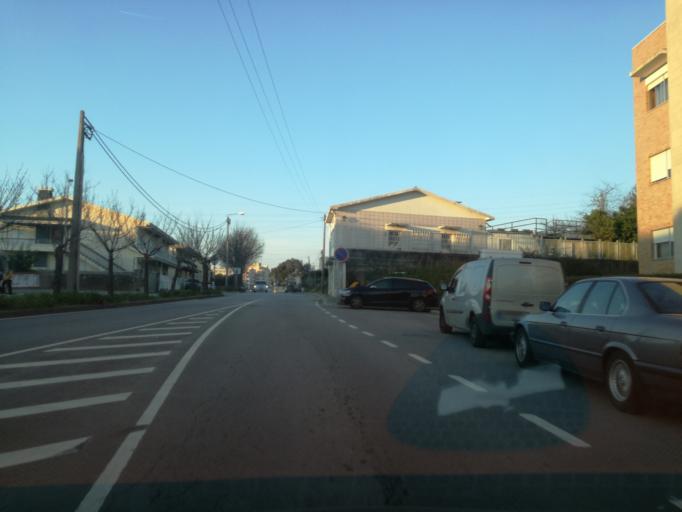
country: PT
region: Porto
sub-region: Maia
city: Milheiros
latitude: 41.2255
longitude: -8.5890
